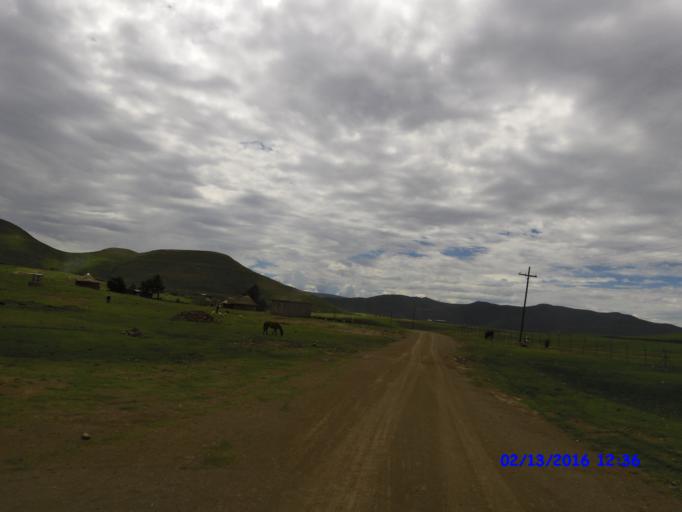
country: LS
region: Maseru
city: Nako
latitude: -29.8410
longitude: 28.0236
